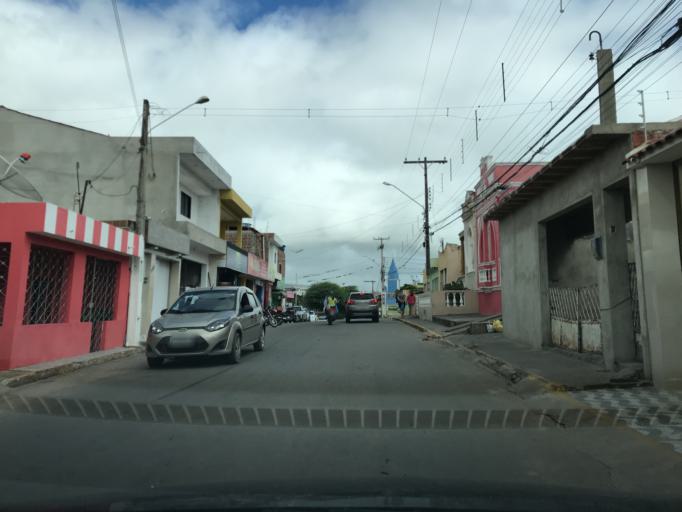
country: BR
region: Pernambuco
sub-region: Bezerros
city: Bezerros
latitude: -8.2315
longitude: -35.7520
